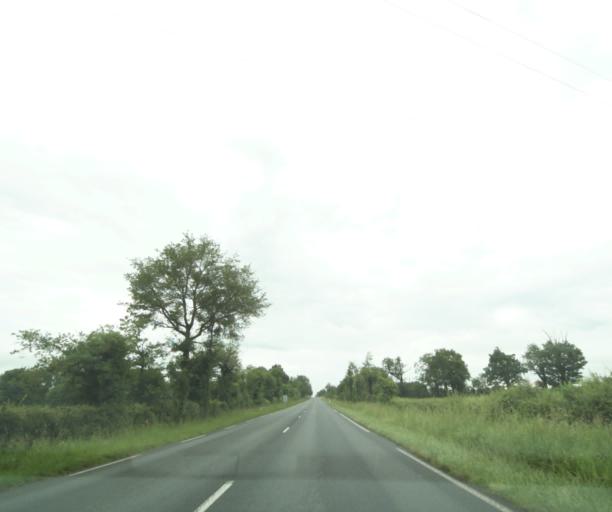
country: FR
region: Poitou-Charentes
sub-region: Departement des Deux-Sevres
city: Viennay
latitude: 46.7209
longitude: -0.2384
